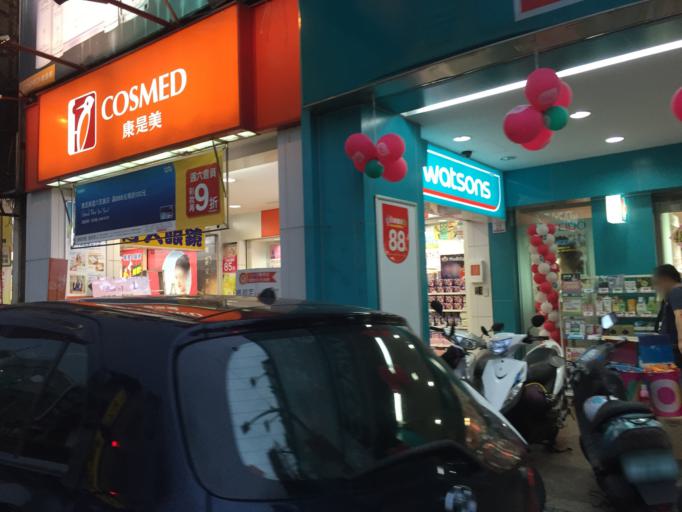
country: TW
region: Taiwan
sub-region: Yilan
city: Yilan
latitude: 24.7559
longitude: 121.7522
